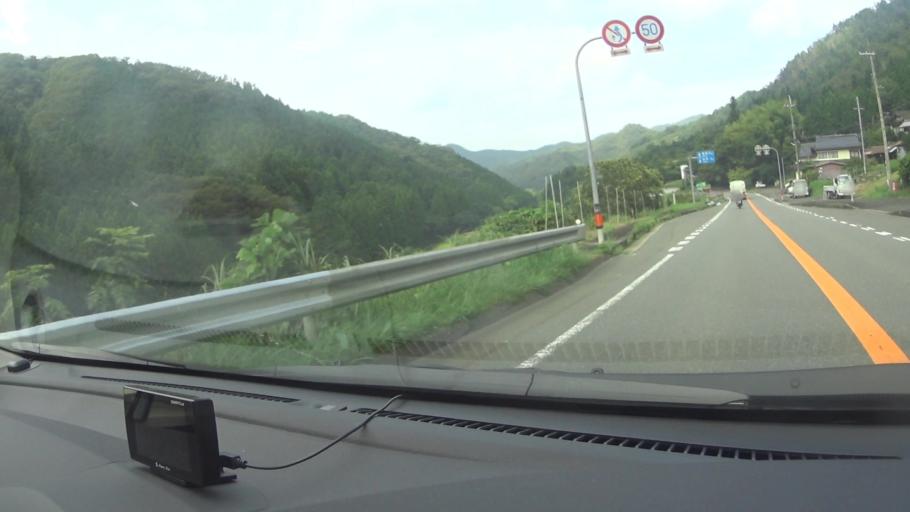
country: JP
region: Kyoto
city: Ayabe
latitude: 35.2453
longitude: 135.2848
